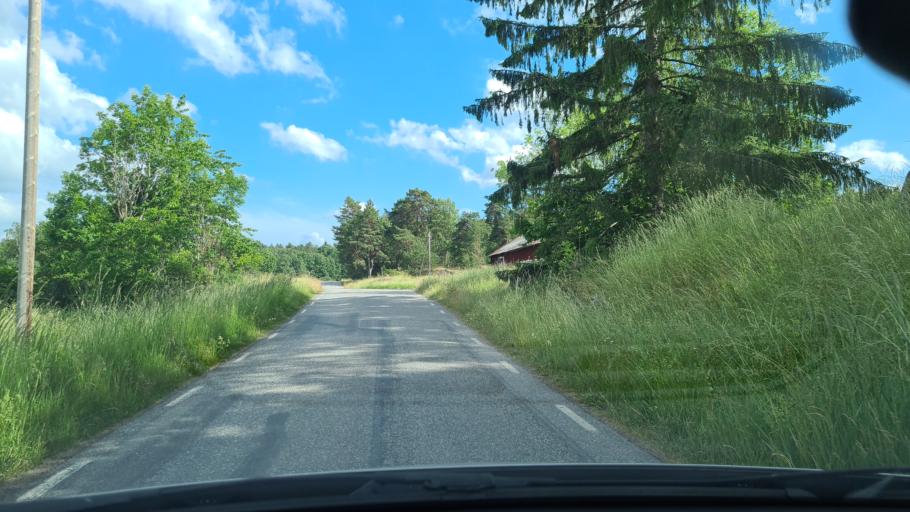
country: SE
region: Stockholm
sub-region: Varmdo Kommun
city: Mortnas
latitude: 59.4082
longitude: 18.4548
